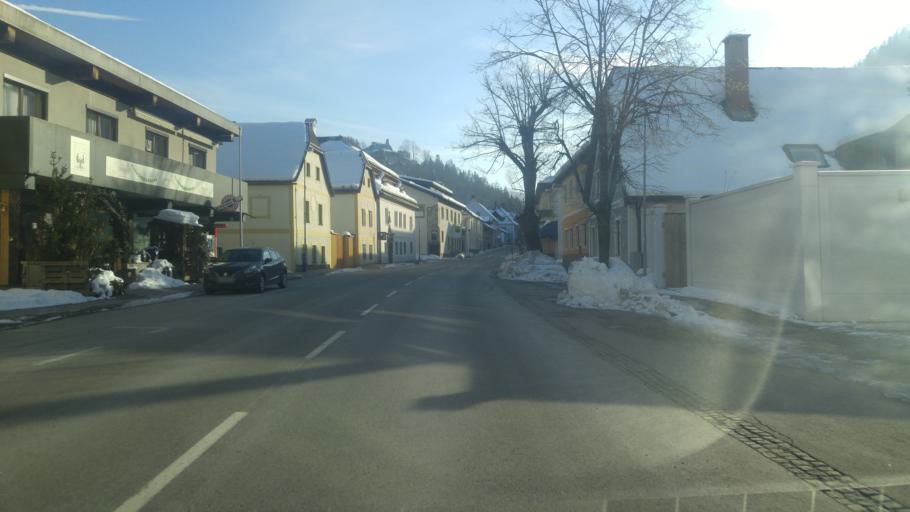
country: AT
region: Lower Austria
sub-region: Politischer Bezirk Lilienfeld
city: Hohenberg
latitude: 47.9101
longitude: 15.6193
